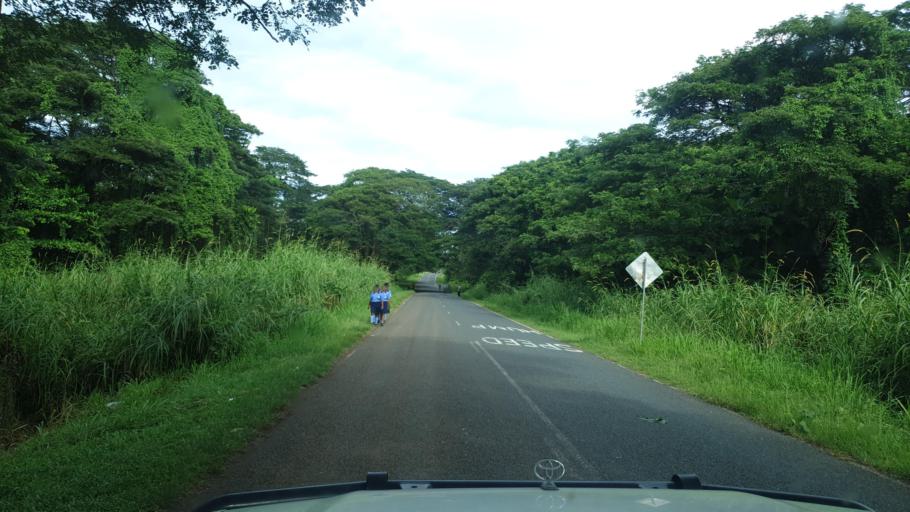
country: PG
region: National Capital
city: Port Moresby
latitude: -8.9955
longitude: 146.9849
